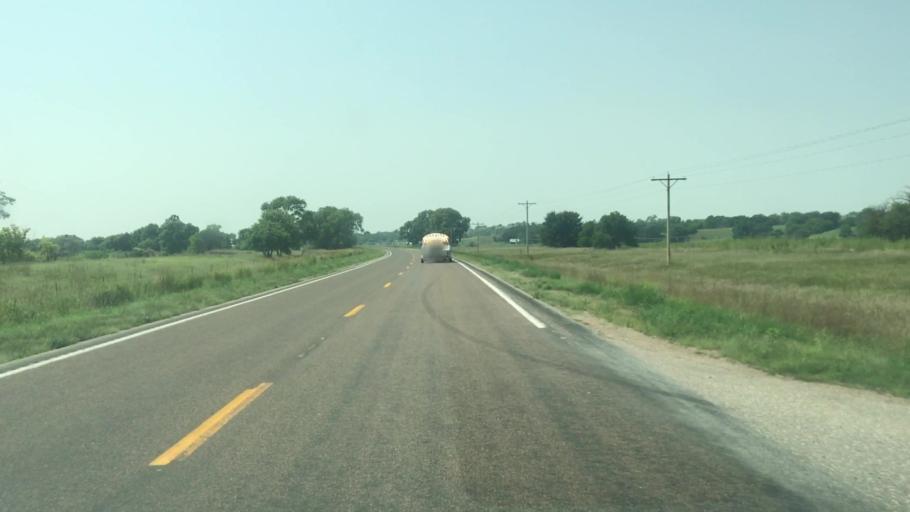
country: US
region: Nebraska
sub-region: Buffalo County
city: Ravenna
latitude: 41.0766
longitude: -98.6913
